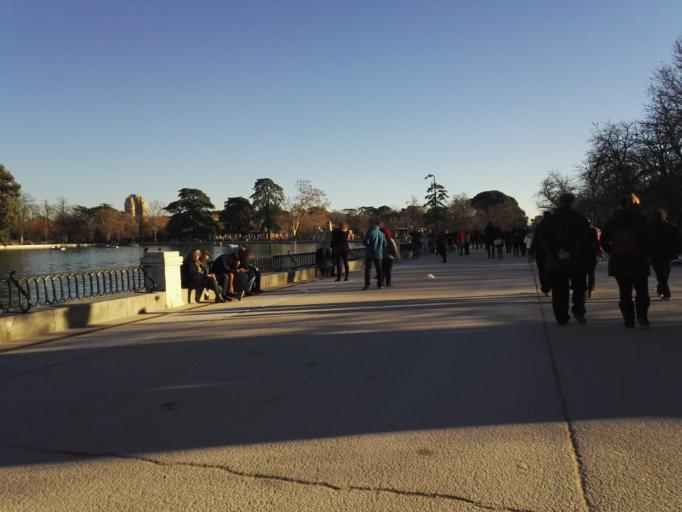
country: ES
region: Madrid
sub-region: Provincia de Madrid
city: Retiro
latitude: 40.4171
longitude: -3.6848
